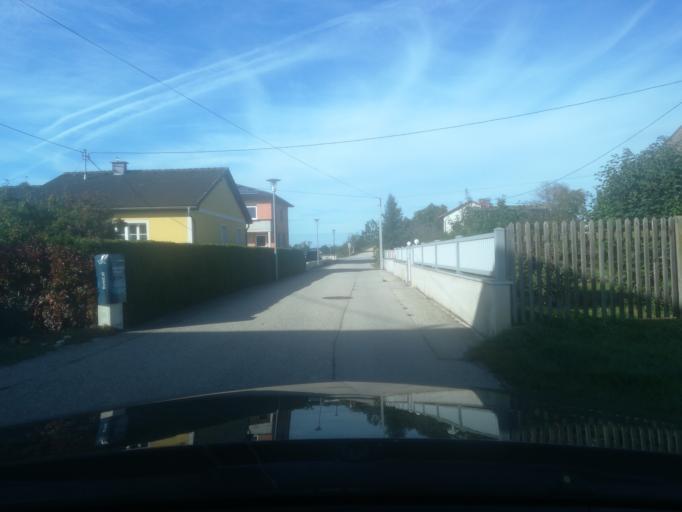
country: AT
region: Upper Austria
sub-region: Wels-Land
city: Marchtrenk
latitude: 48.2049
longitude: 14.1459
